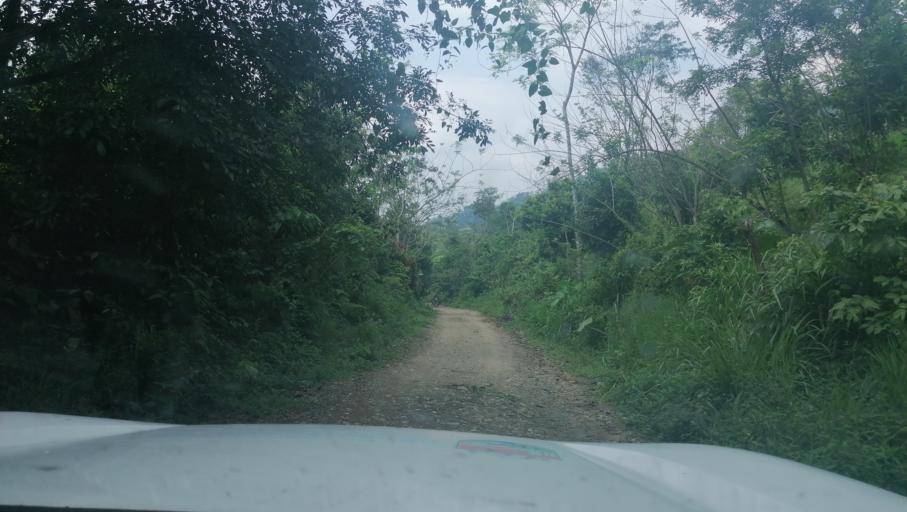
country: MX
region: Chiapas
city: Ostuacan
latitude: 17.3606
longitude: -93.3246
